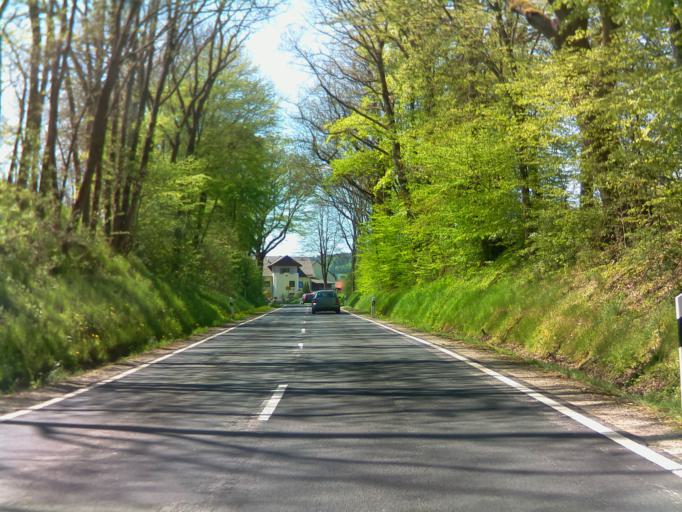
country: DE
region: Hesse
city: Grebenau
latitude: 50.7788
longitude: 9.4837
